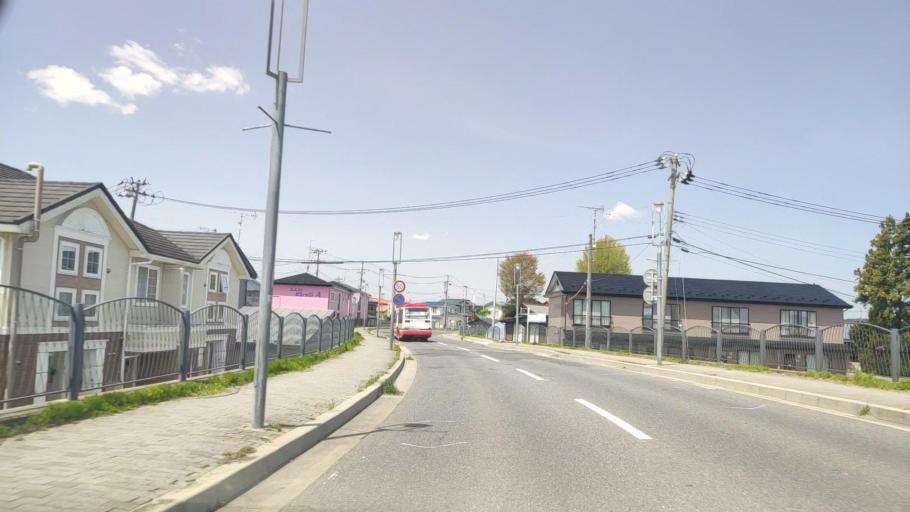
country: JP
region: Aomori
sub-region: Hachinohe Shi
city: Uchimaru
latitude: 40.5027
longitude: 141.4418
